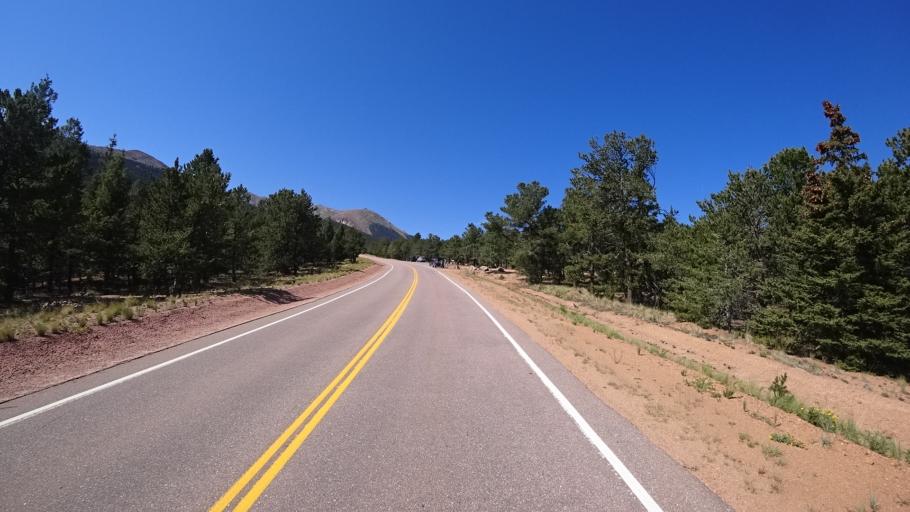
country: US
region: Colorado
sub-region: El Paso County
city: Cascade-Chipita Park
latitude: 38.9022
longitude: -105.0643
